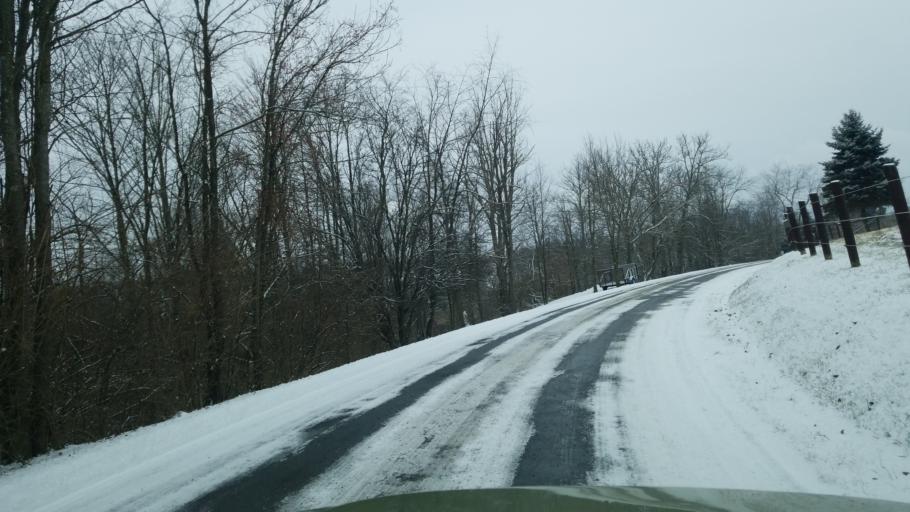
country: US
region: Pennsylvania
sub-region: Centre County
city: Centre Hall
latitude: 40.7816
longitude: -77.6770
